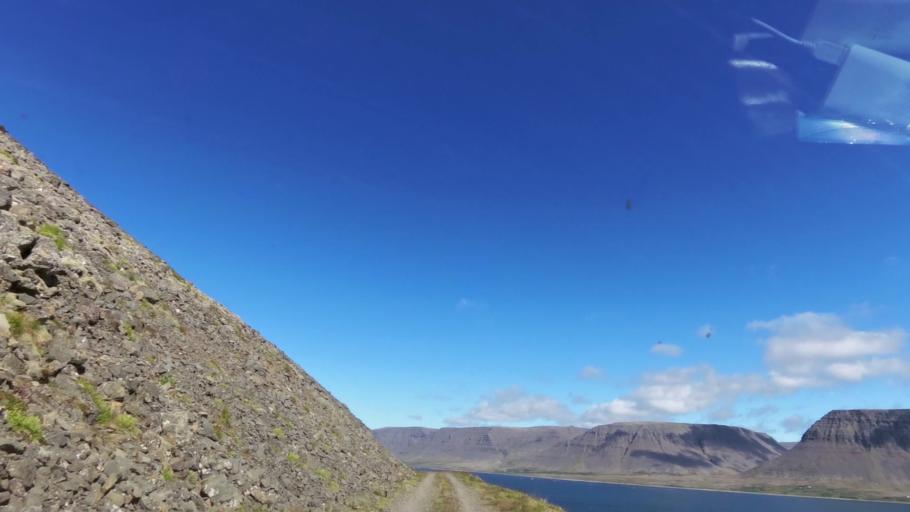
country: IS
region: West
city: Olafsvik
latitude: 65.6319
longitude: -23.9166
